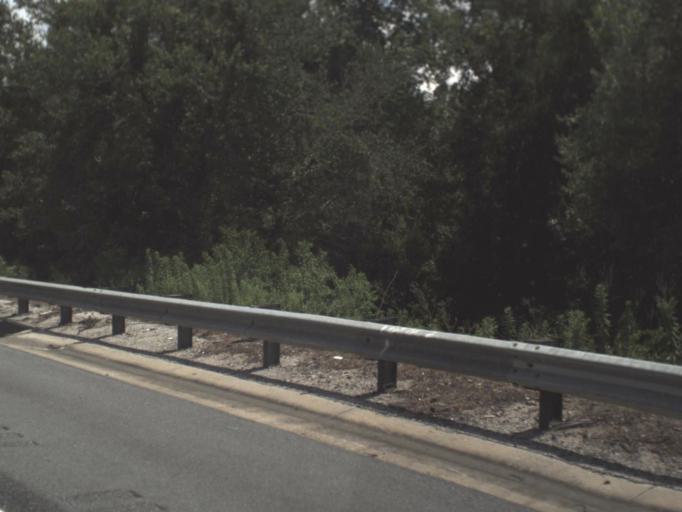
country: US
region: Florida
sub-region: Hamilton County
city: Jasper
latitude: 30.4559
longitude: -82.9451
